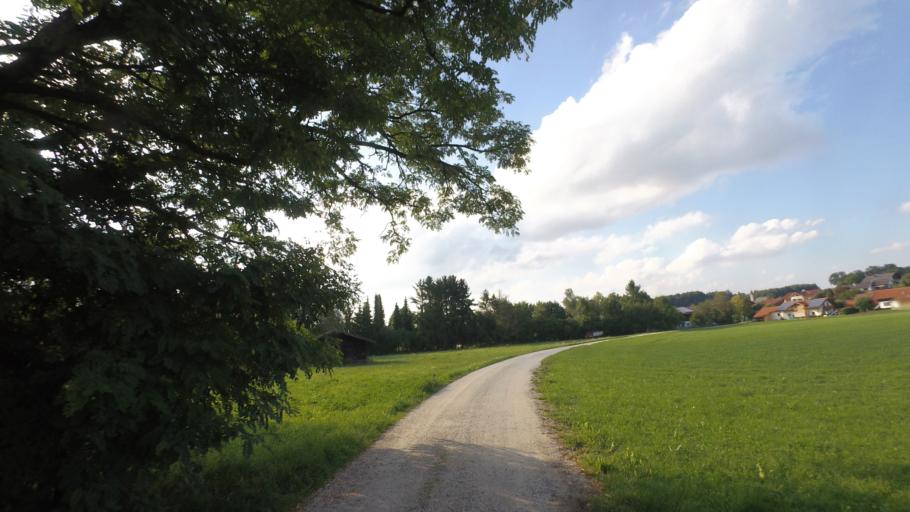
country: DE
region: Bavaria
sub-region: Upper Bavaria
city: Chieming
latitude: 47.9073
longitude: 12.5596
